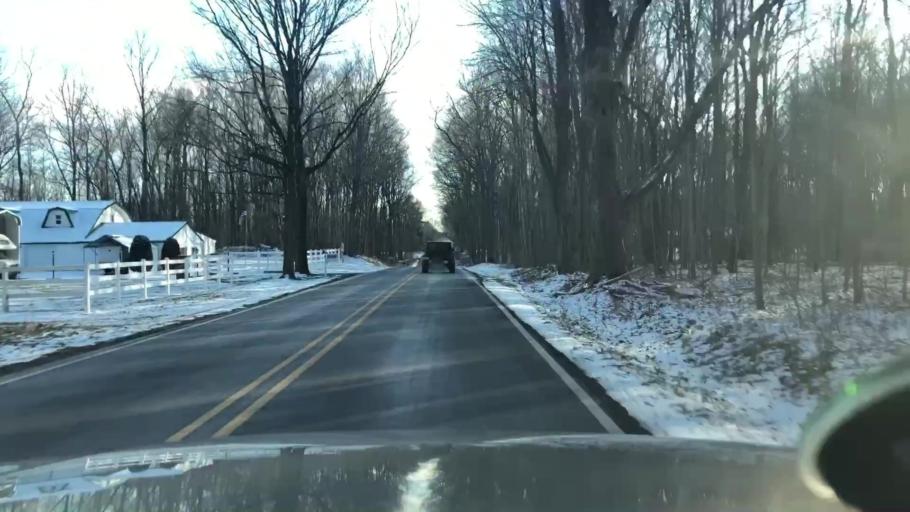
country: US
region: Michigan
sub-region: Jackson County
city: Vandercook Lake
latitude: 42.1112
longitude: -84.4513
